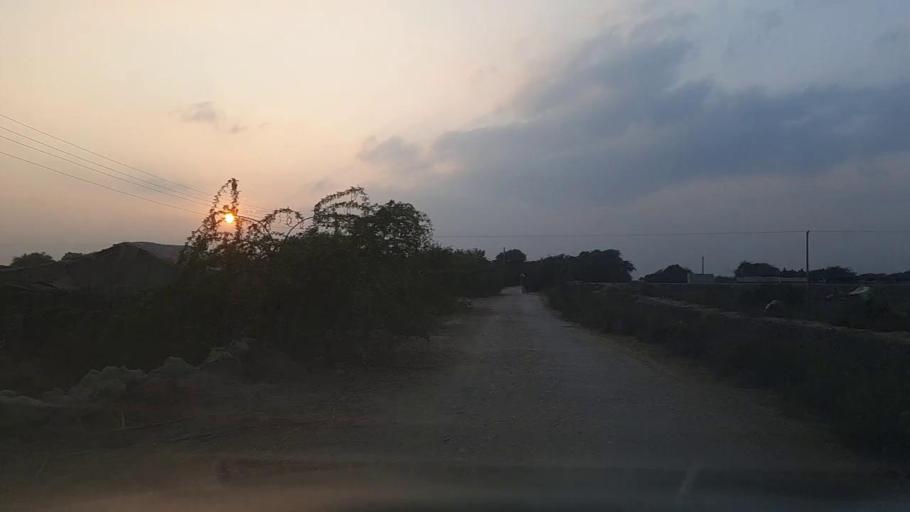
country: PK
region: Sindh
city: Jati
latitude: 24.5298
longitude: 68.3853
